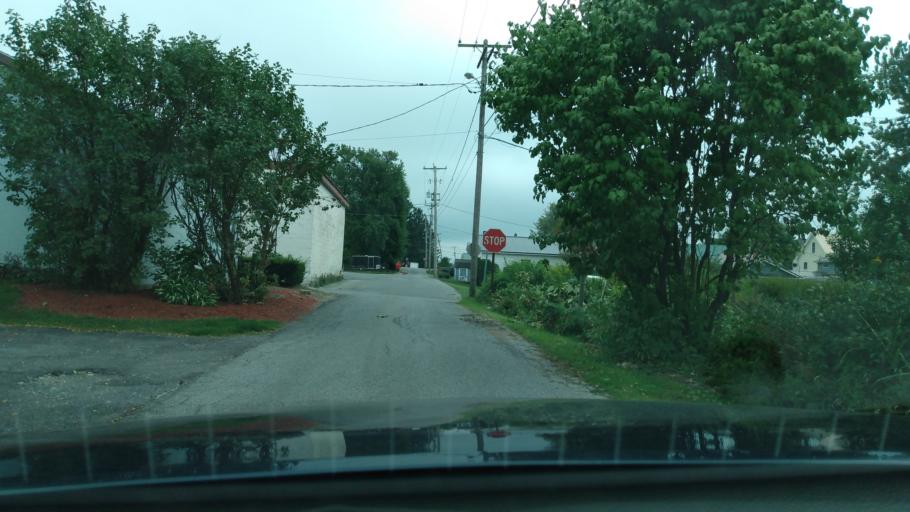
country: US
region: Pennsylvania
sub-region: Cambria County
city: Hastings
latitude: 40.6046
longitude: -78.7099
